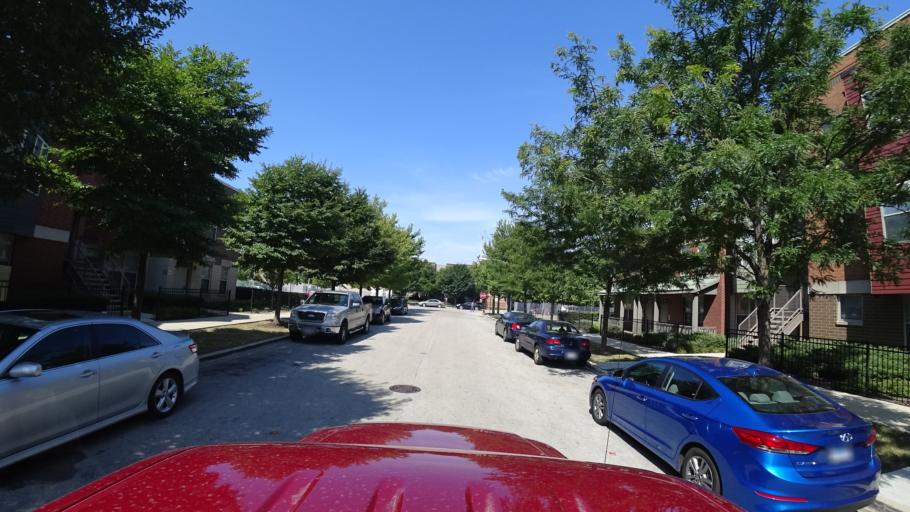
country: US
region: Illinois
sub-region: Cook County
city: Chicago
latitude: 41.8204
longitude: -87.6278
